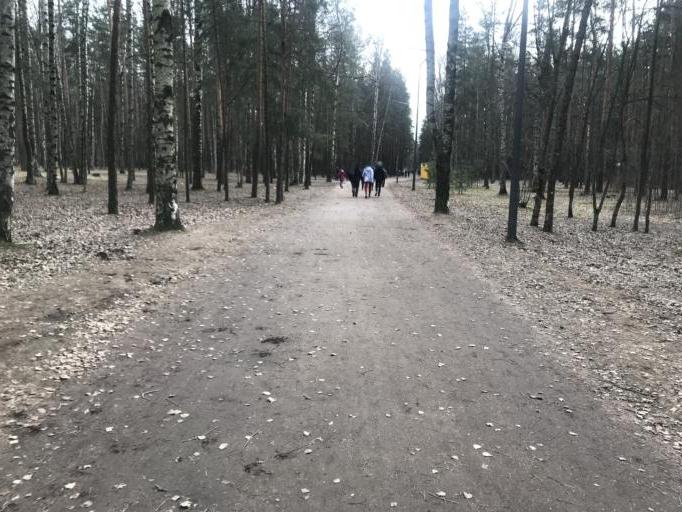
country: RU
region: St.-Petersburg
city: Sosnovka
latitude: 60.0167
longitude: 30.3483
